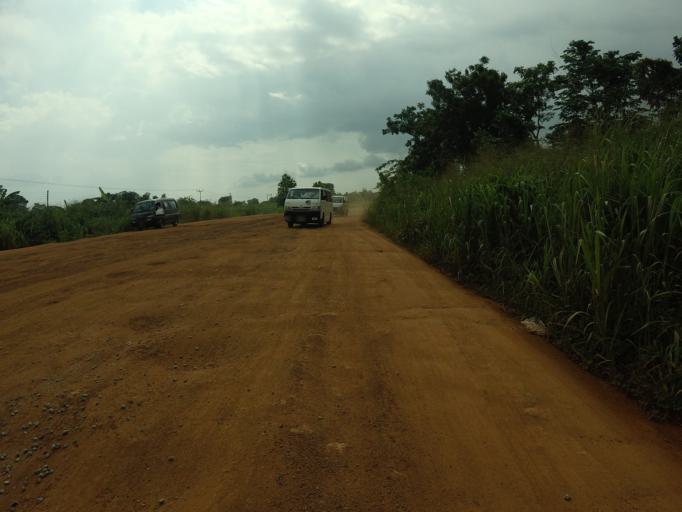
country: GH
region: Volta
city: Kpandu
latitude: 6.9898
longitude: 0.4410
